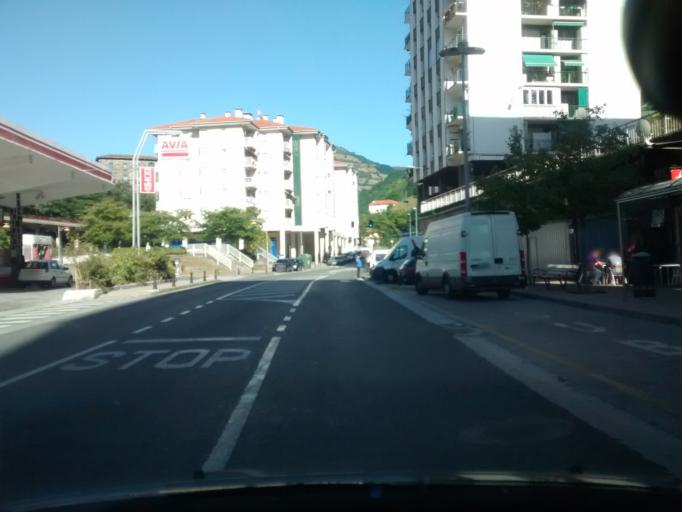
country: ES
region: Basque Country
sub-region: Provincia de Guipuzcoa
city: Eibar
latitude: 43.1898
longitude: -2.4549
